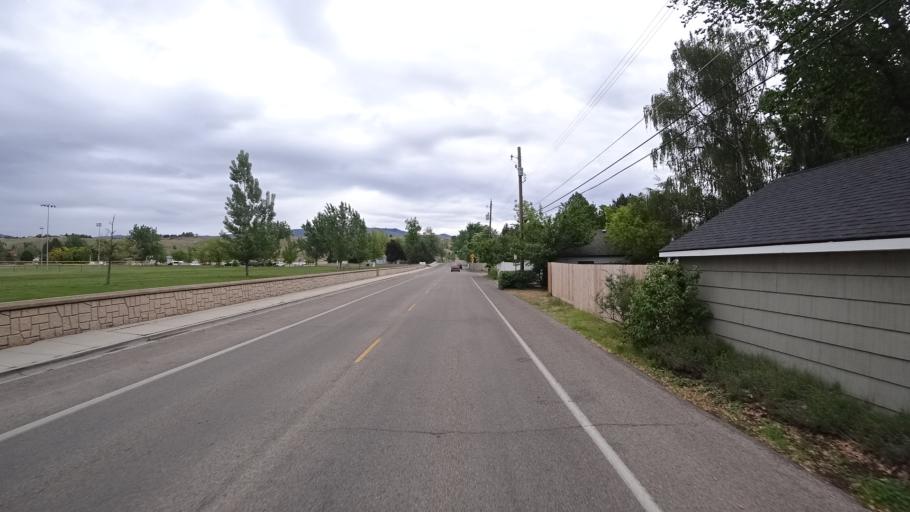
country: US
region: Idaho
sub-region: Ada County
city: Boise
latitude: 43.6138
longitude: -116.1884
